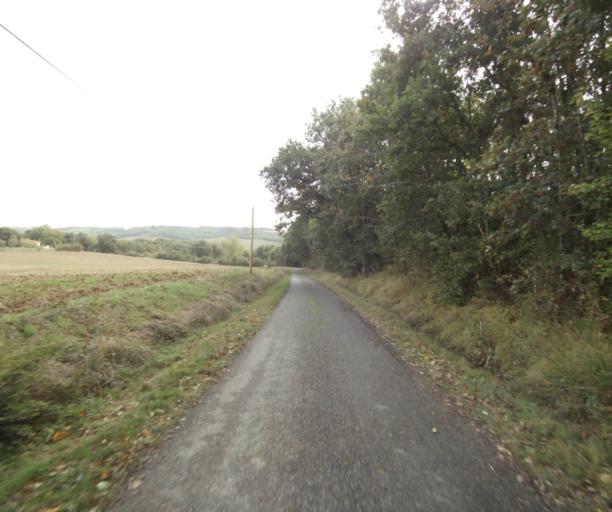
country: FR
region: Midi-Pyrenees
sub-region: Departement du Tarn-et-Garonne
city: Beaumont-de-Lomagne
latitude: 43.8705
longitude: 1.1009
